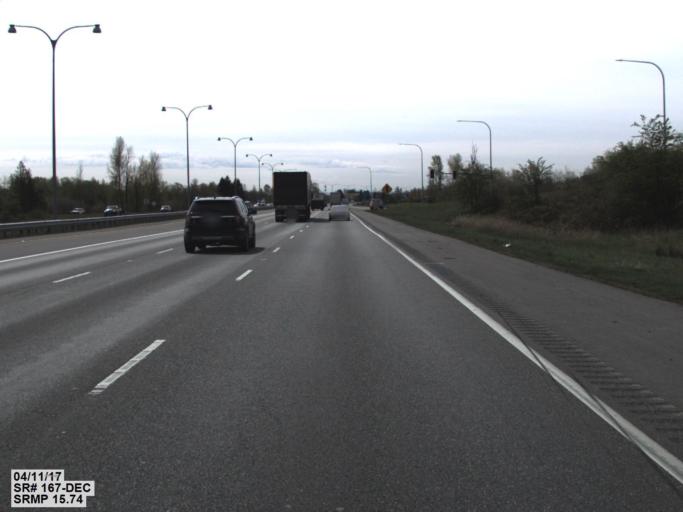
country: US
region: Washington
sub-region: King County
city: Auburn
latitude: 47.3219
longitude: -122.2452
